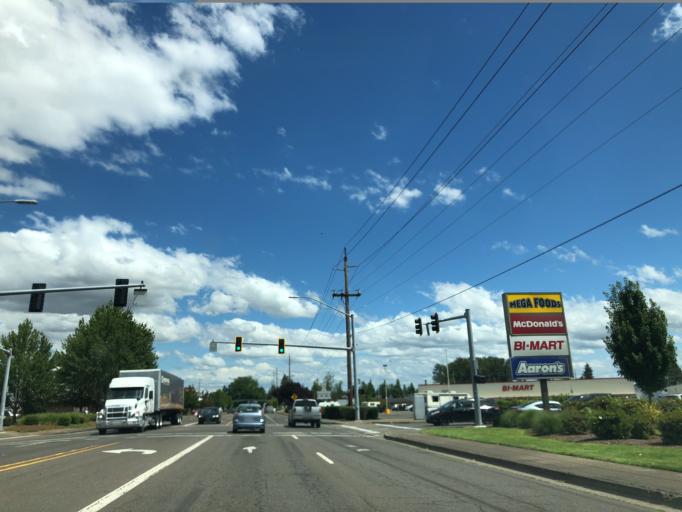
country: US
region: Oregon
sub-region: Marion County
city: Woodburn
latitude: 45.1514
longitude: -122.8366
